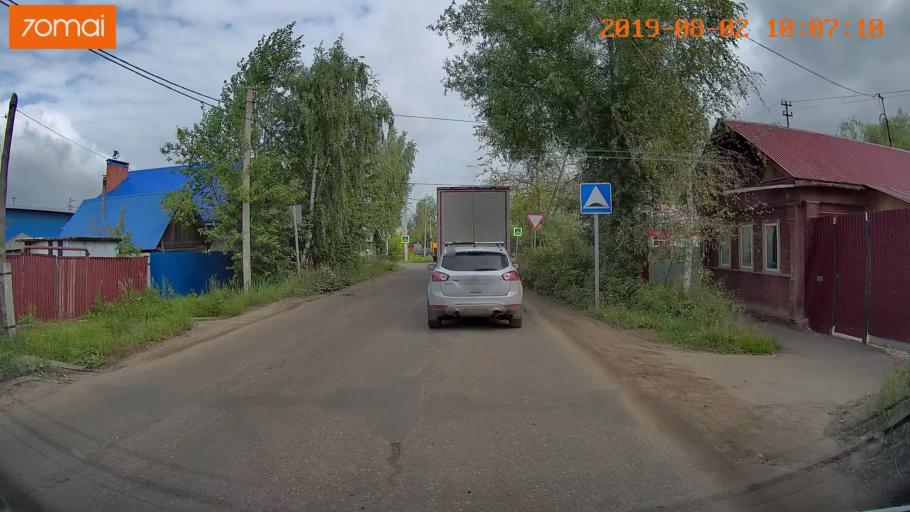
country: RU
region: Ivanovo
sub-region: Gorod Ivanovo
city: Ivanovo
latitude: 56.9818
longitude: 40.9358
